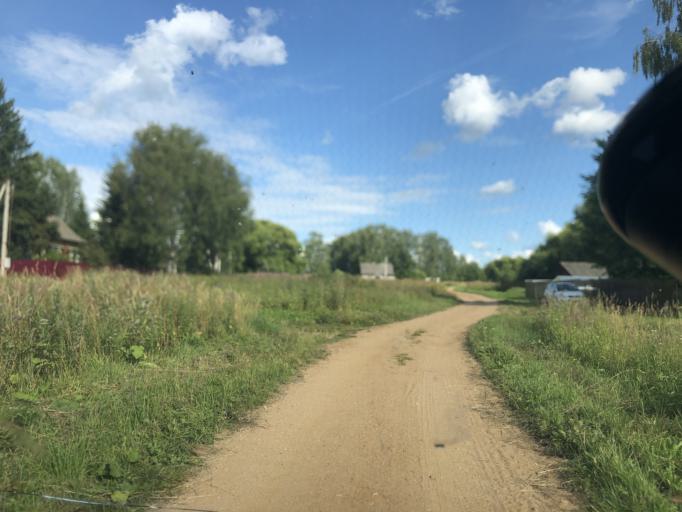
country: RU
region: Smolensk
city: Ugra
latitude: 54.8508
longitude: 34.5016
